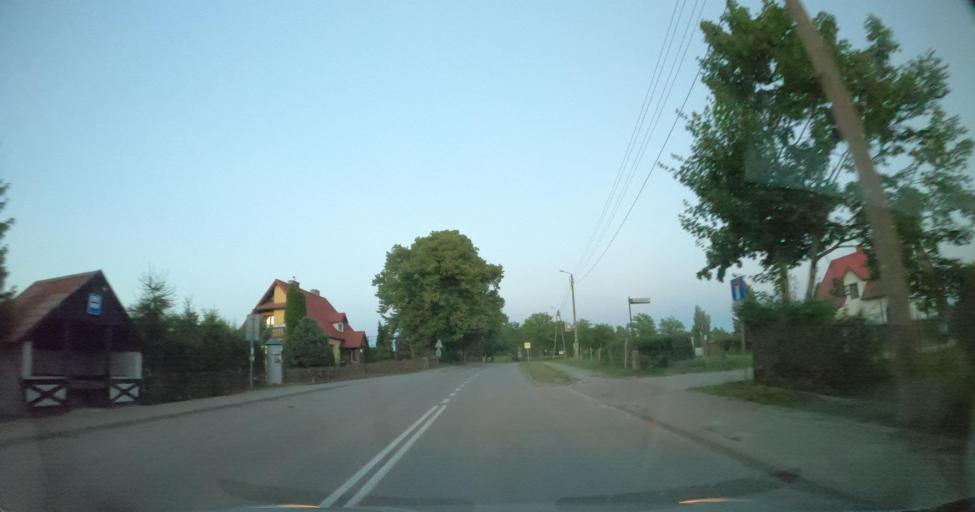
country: PL
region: Pomeranian Voivodeship
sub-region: Powiat wejherowski
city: Szemud
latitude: 54.4775
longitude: 18.2693
